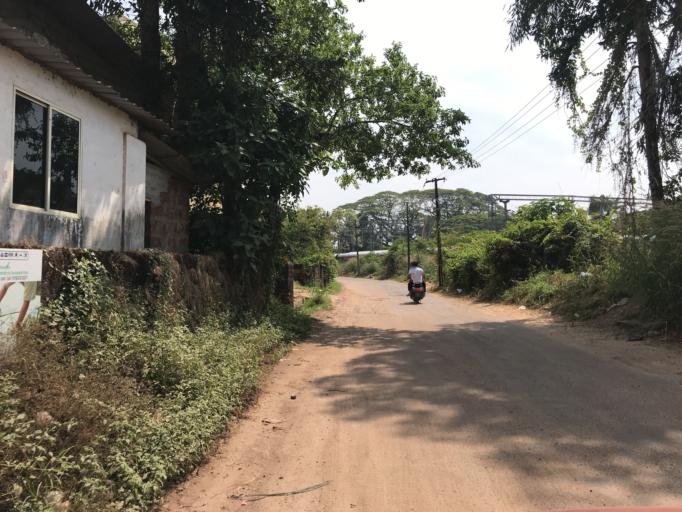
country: IN
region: Karnataka
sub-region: Dakshina Kannada
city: Ullal
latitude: 12.8547
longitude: 74.8355
